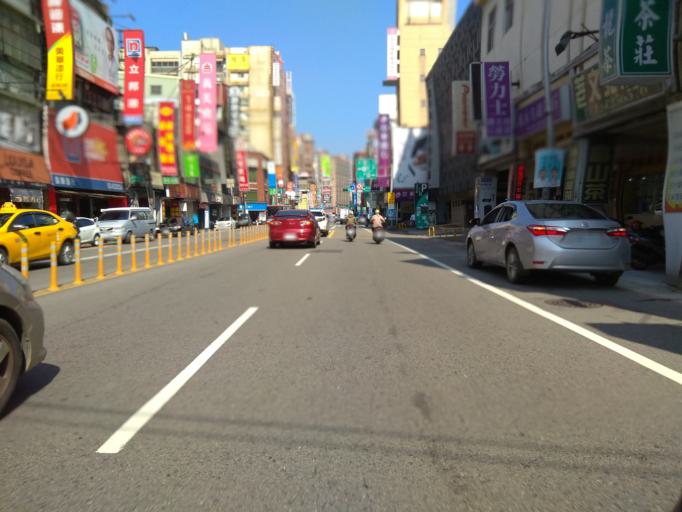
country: TW
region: Taiwan
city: Taoyuan City
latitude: 24.9558
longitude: 121.2230
